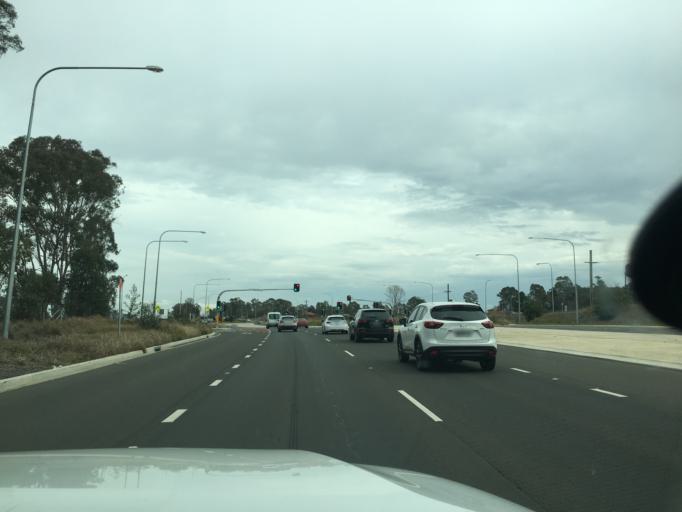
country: AU
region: New South Wales
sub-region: Campbelltown Municipality
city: Denham Court
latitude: -33.9815
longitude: 150.8005
